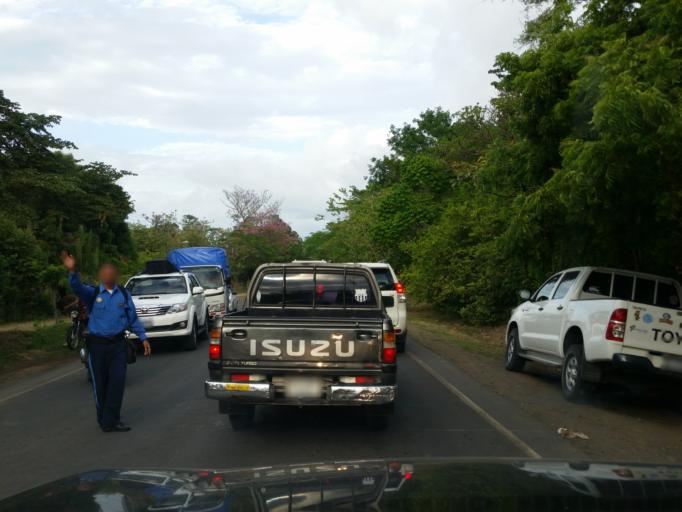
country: NI
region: Rivas
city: Rivas
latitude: 11.4417
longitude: -85.8459
